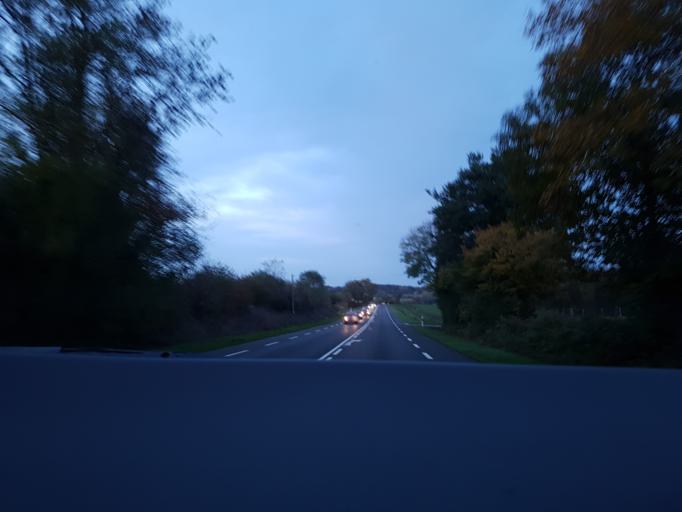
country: FR
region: Pays de la Loire
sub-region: Departement de la Mayenne
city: Montigne-le-Brillant
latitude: 48.0028
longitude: -0.8404
